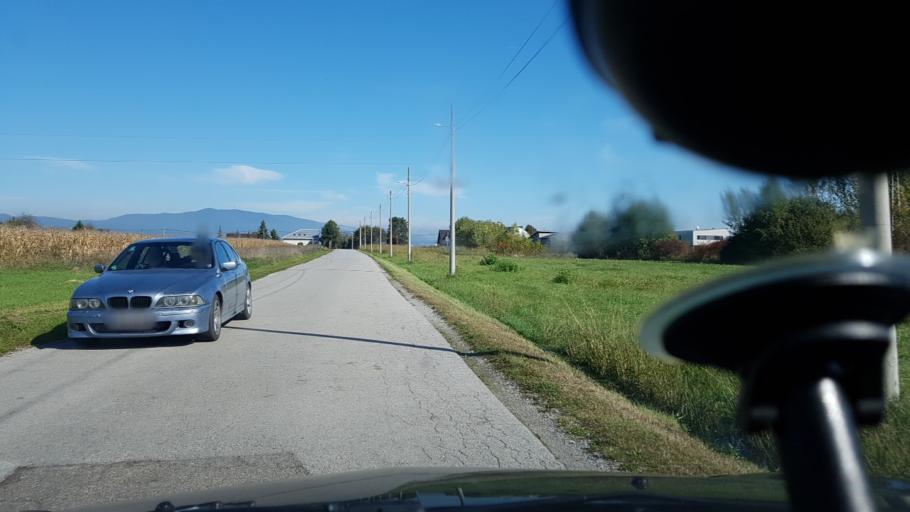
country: HR
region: Grad Zagreb
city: Lucko
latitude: 45.7437
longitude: 15.8650
